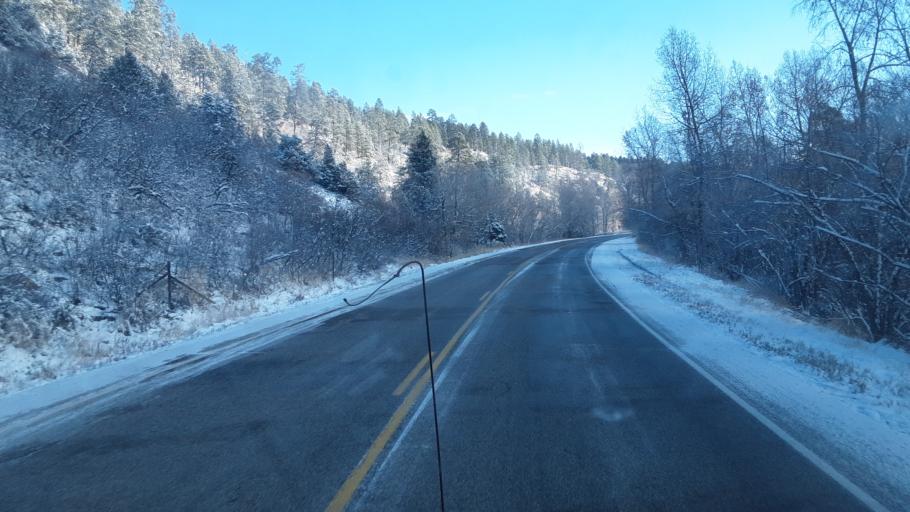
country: US
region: Colorado
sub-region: La Plata County
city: Durango
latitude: 37.3245
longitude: -107.7621
